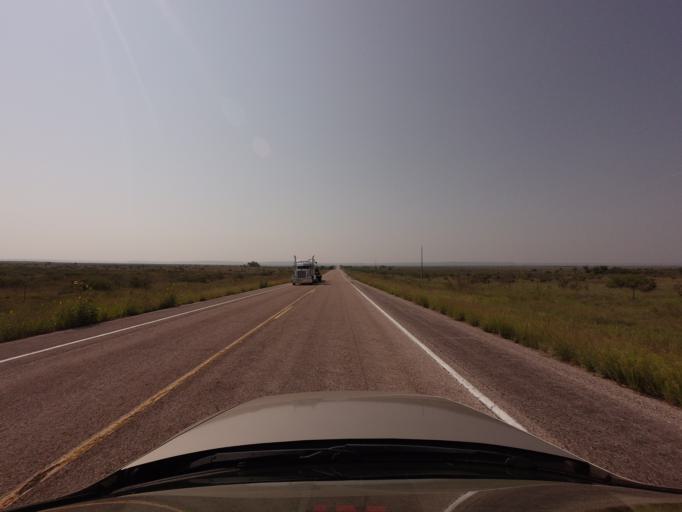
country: US
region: New Mexico
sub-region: Quay County
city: Tucumcari
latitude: 34.9437
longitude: -103.7602
